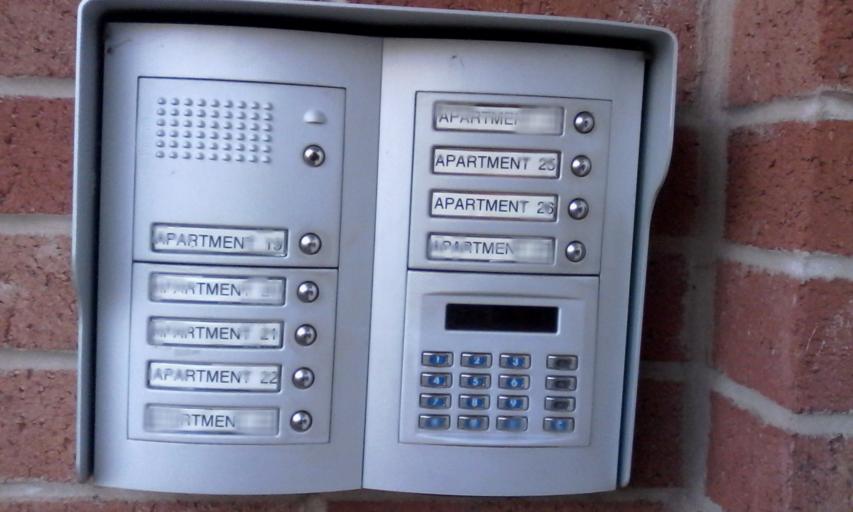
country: GB
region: England
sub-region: Nottinghamshire
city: Arnold
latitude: 52.9904
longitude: -1.1099
